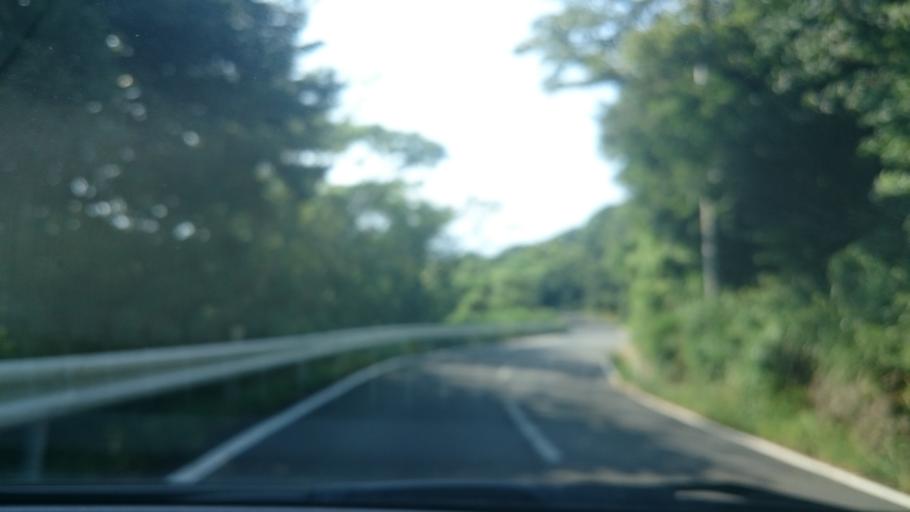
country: JP
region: Shizuoka
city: Heda
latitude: 34.9662
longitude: 138.7675
